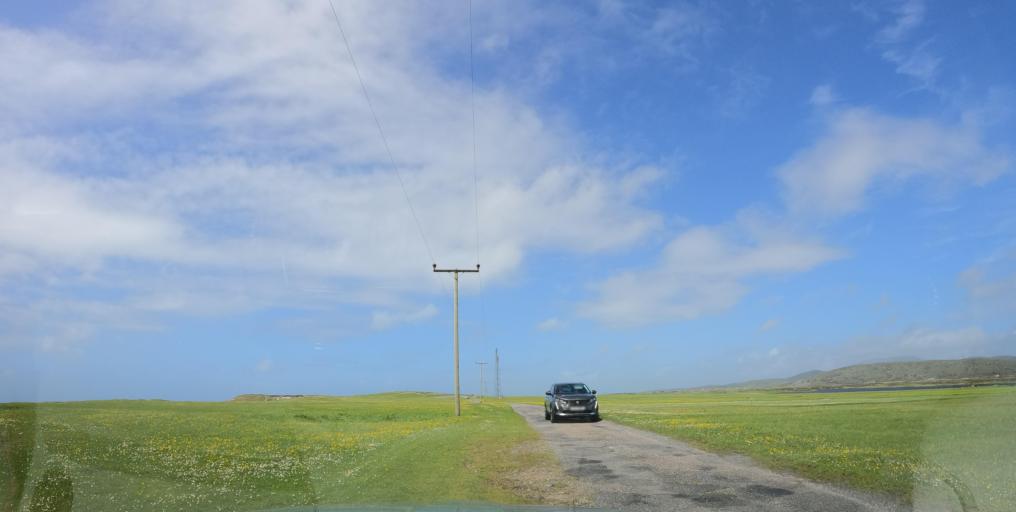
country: GB
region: Scotland
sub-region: Eilean Siar
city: Isle of South Uist
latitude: 57.1663
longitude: -7.4005
